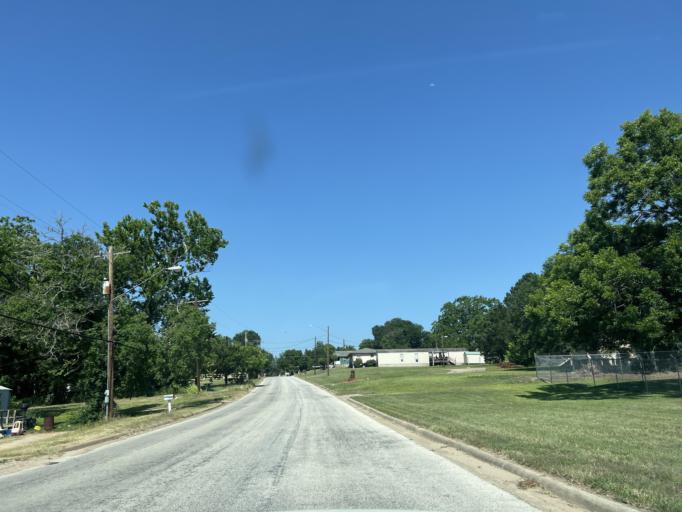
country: US
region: Texas
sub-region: Washington County
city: Brenham
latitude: 30.1702
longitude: -96.3769
